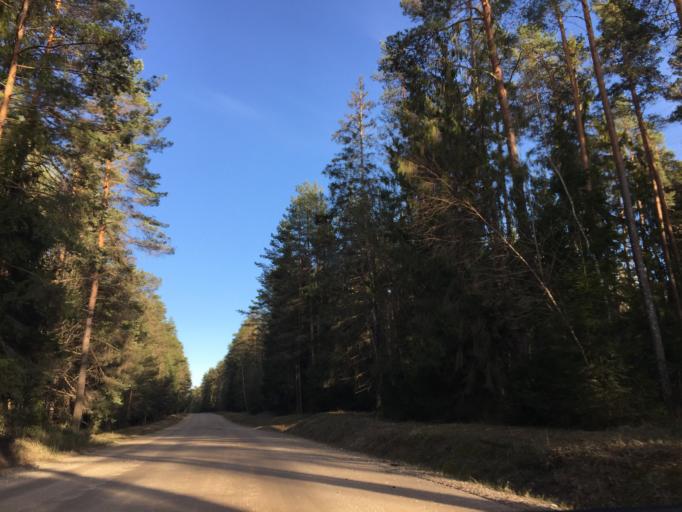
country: LV
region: Valkas Rajons
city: Valka
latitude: 57.7958
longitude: 25.9651
